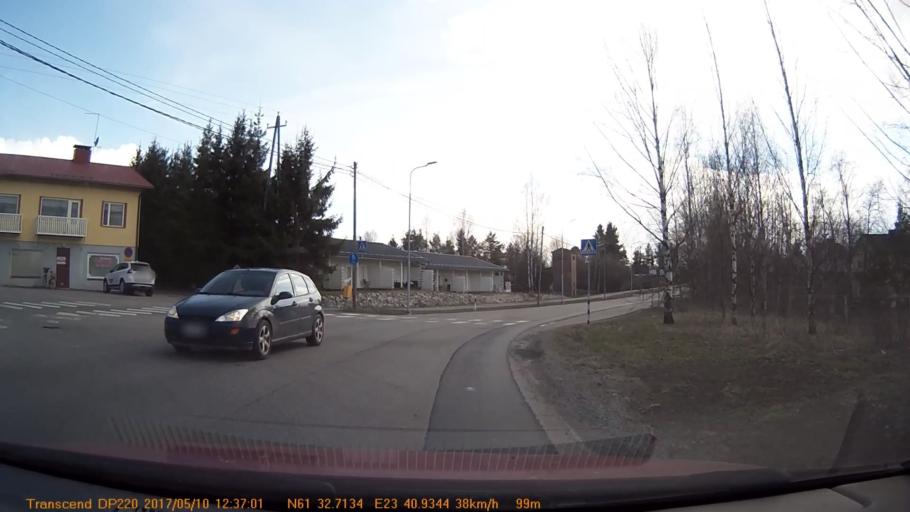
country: FI
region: Pirkanmaa
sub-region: Tampere
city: Yloejaervi
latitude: 61.5452
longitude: 23.6821
